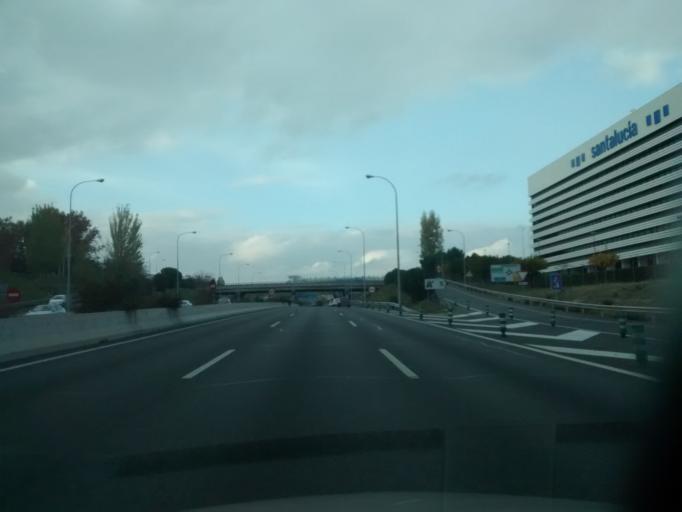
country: ES
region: Madrid
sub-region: Provincia de Madrid
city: Hortaleza
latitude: 40.4667
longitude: -3.6264
